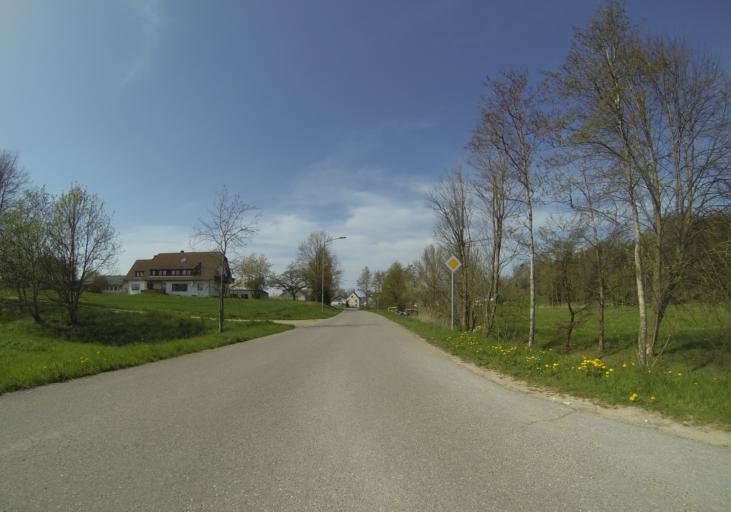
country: DE
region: Baden-Wuerttemberg
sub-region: Tuebingen Region
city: Huttisheim
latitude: 48.2734
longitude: 9.9468
